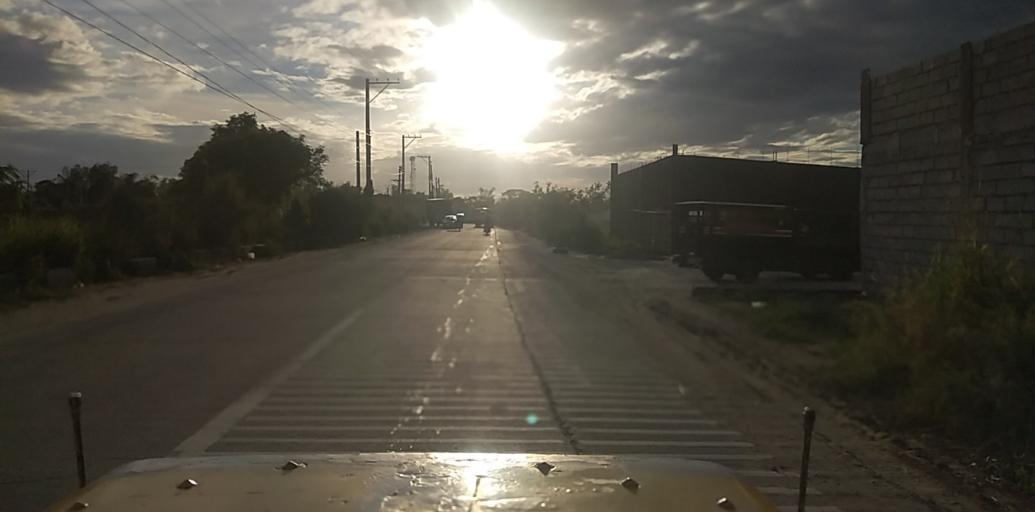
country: PH
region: Central Luzon
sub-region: Province of Pampanga
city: Malino
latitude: 15.1322
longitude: 120.6780
